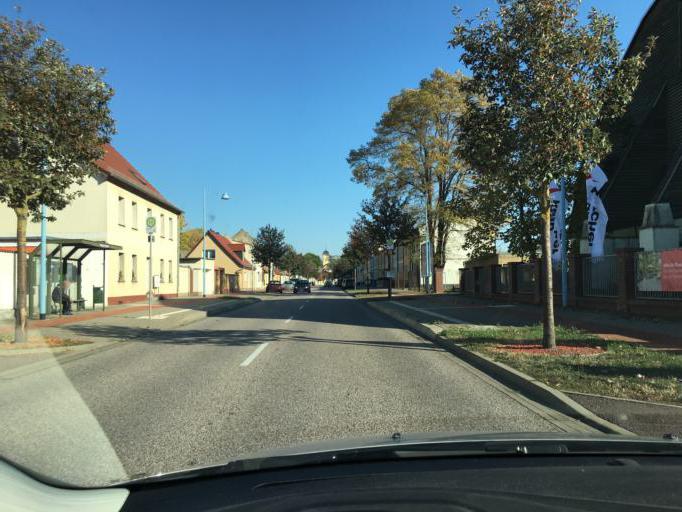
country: DE
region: Saxony-Anhalt
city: Bernburg
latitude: 51.7991
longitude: 11.7677
